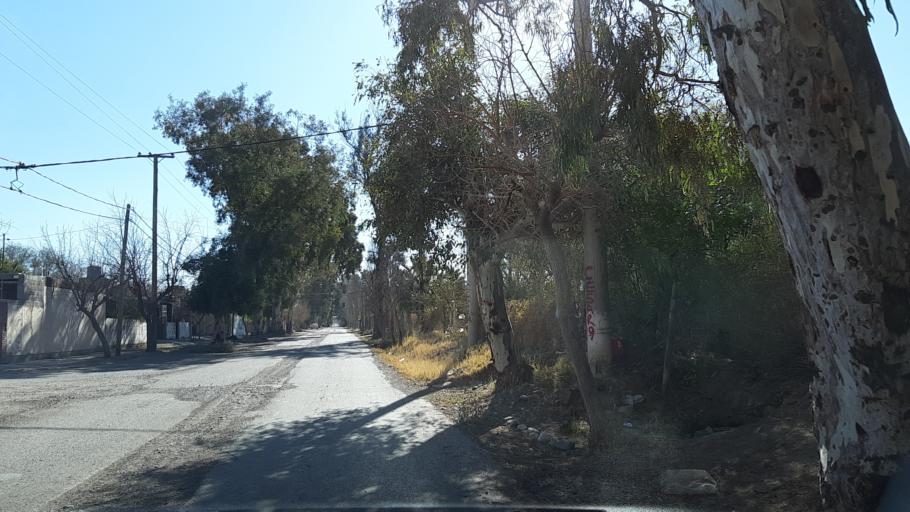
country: AR
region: San Juan
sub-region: Departamento de Zonda
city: Zonda
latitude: -31.5493
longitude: -68.7271
